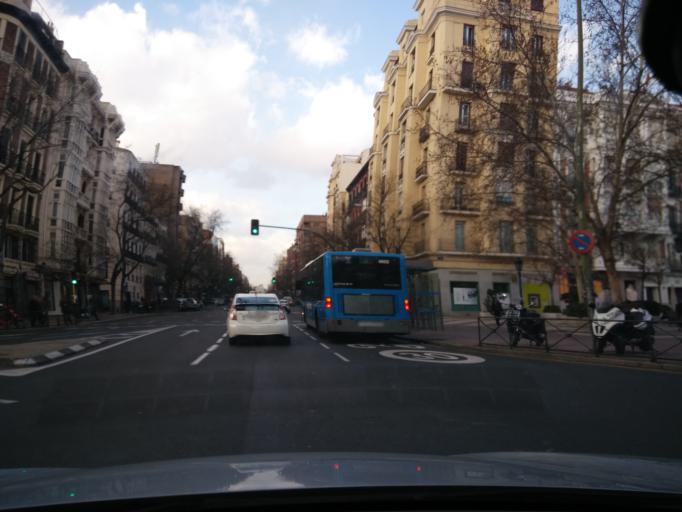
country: ES
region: Madrid
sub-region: Provincia de Madrid
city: Chamberi
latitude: 40.4324
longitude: -3.6977
